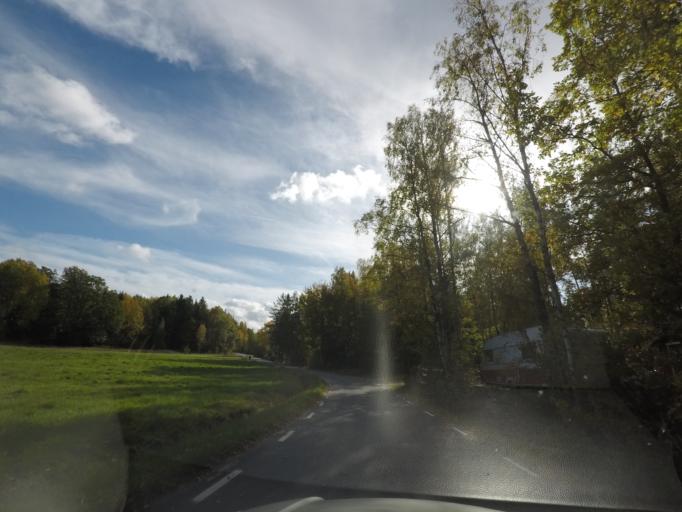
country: SE
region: Soedermanland
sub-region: Eskilstuna Kommun
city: Kvicksund
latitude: 59.3225
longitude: 16.2430
